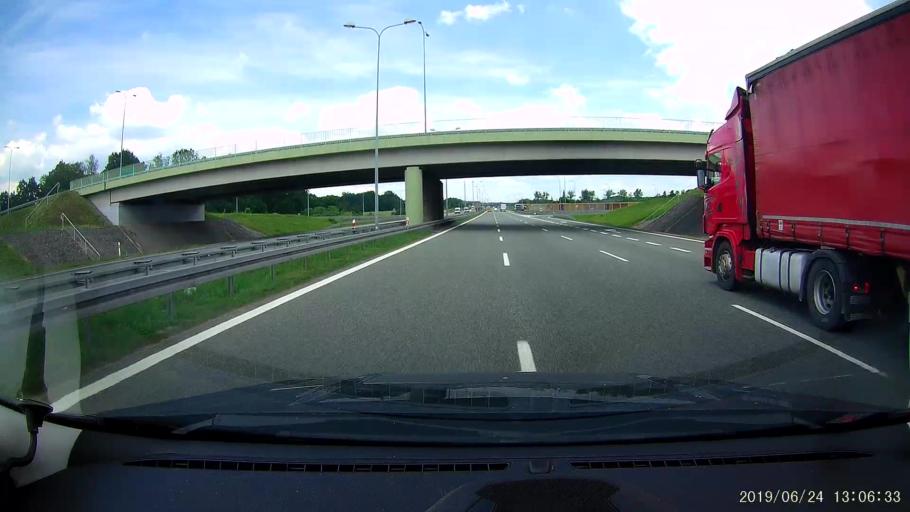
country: PL
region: Silesian Voivodeship
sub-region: Powiat rybnicki
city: Stanowice
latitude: 50.1319
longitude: 18.6913
